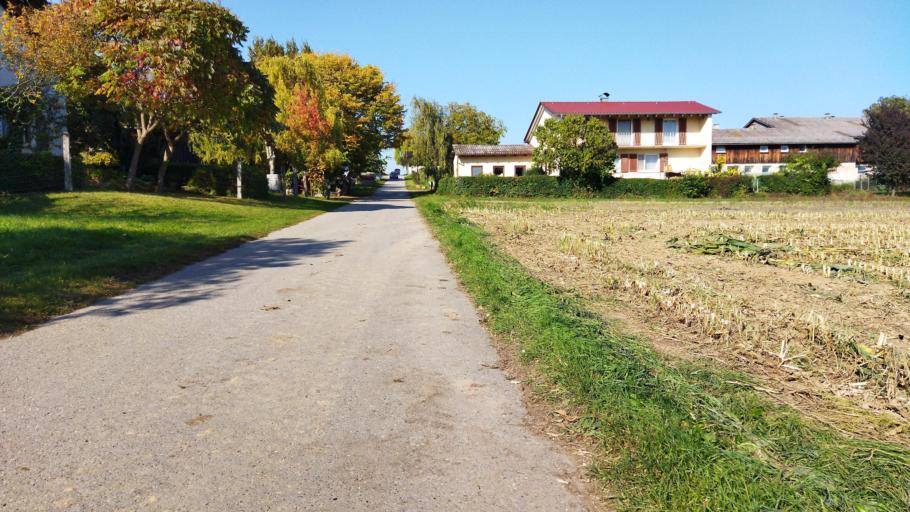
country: DE
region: Baden-Wuerttemberg
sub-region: Regierungsbezirk Stuttgart
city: Erligheim
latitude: 49.0124
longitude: 9.0881
